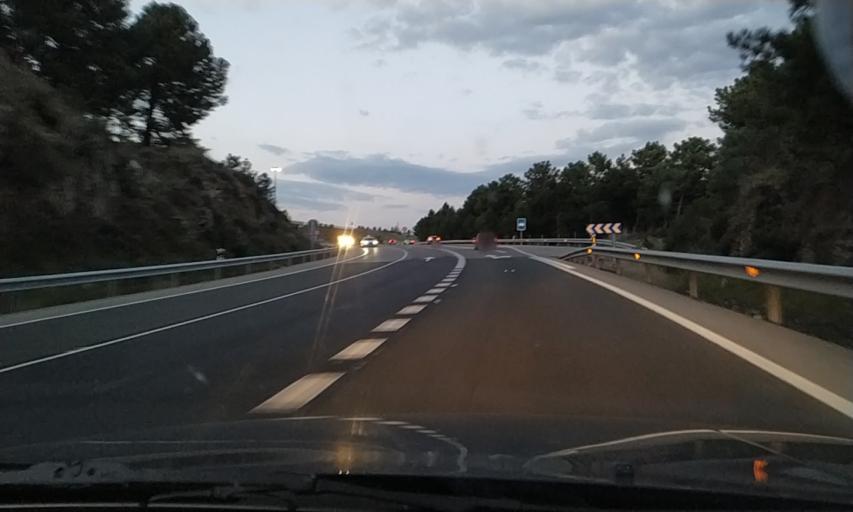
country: ES
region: Castille and Leon
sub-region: Provincia de Leon
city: Molinaseca
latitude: 42.5590
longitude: -6.5556
